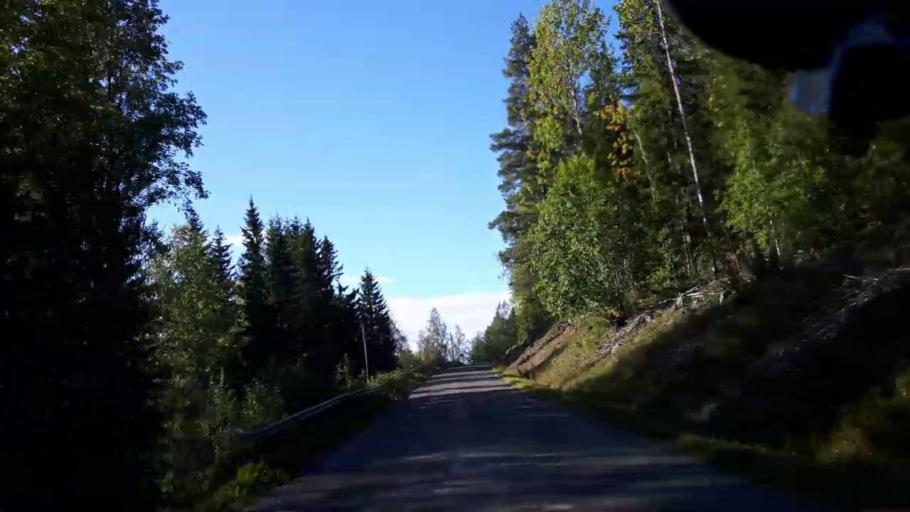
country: SE
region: Jaemtland
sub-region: Ragunda Kommun
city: Hammarstrand
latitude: 63.4933
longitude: 16.0407
